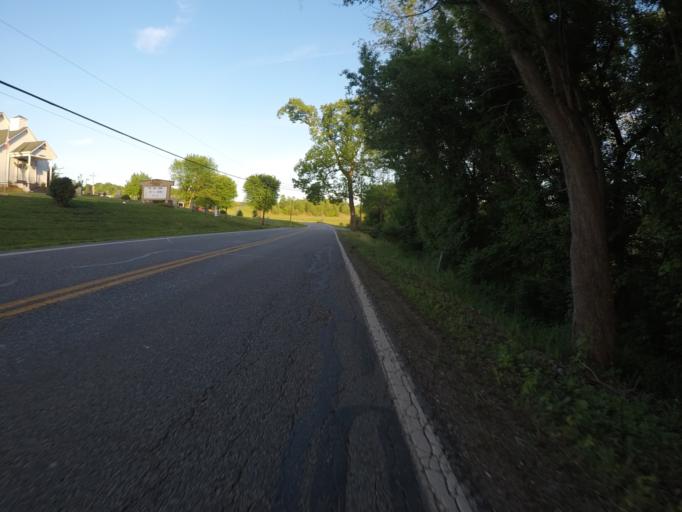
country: US
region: West Virginia
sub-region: Cabell County
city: Huntington
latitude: 38.4868
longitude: -82.4694
